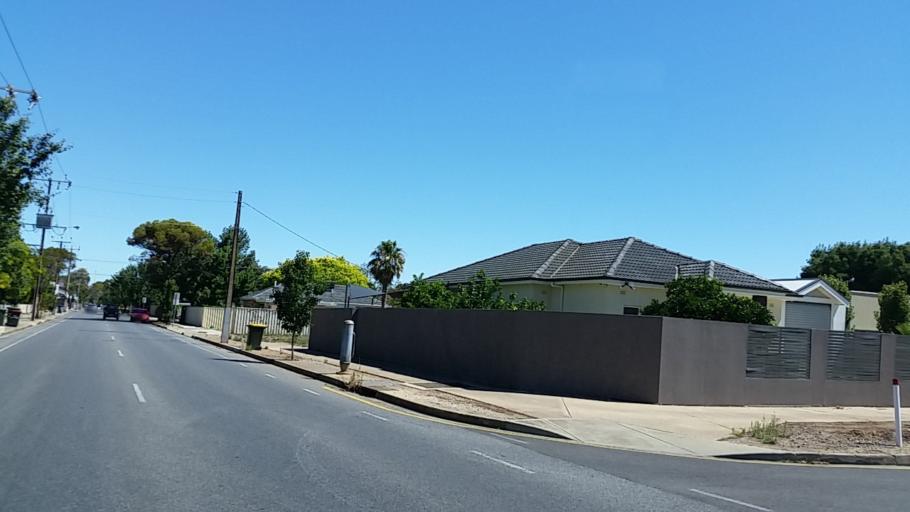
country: AU
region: South Australia
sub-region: Marion
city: South Plympton
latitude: -34.9758
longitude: 138.5646
